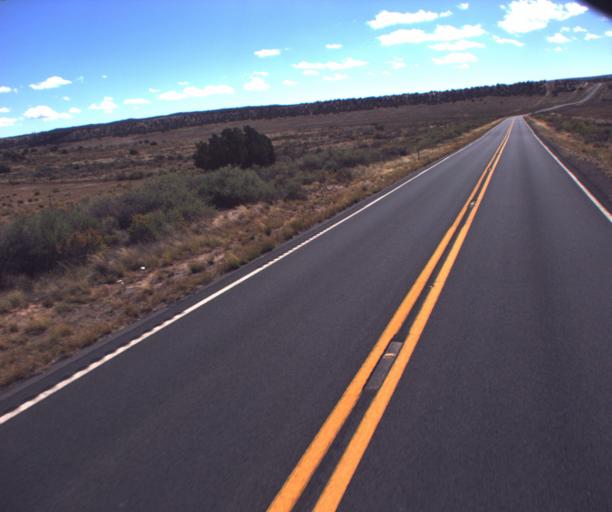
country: US
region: Arizona
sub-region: Apache County
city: Houck
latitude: 35.1016
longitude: -109.3143
